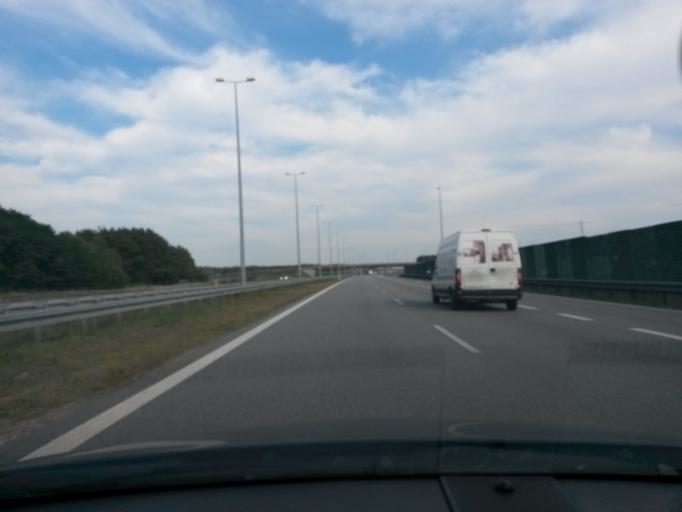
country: PL
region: Greater Poland Voivodeship
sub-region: Powiat koninski
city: Stare Miasto
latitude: 52.1573
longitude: 18.2609
